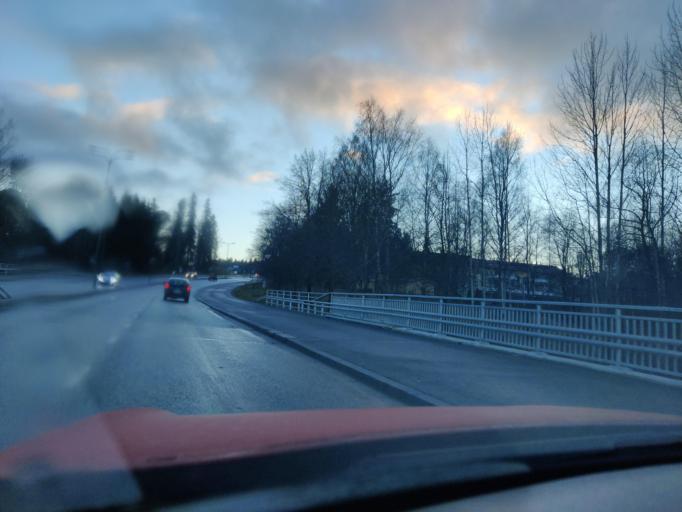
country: FI
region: Pirkanmaa
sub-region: Tampere
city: Nokia
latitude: 61.4727
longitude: 23.5048
